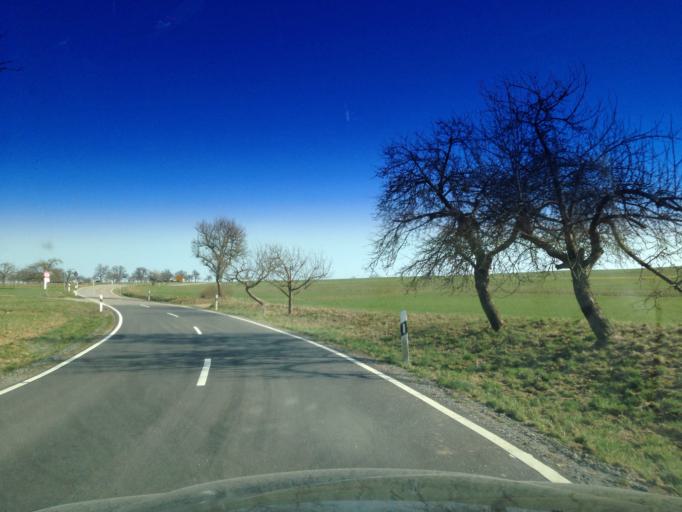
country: DE
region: Baden-Wuerttemberg
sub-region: Karlsruhe Region
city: Illingen
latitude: 48.9249
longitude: 8.9264
